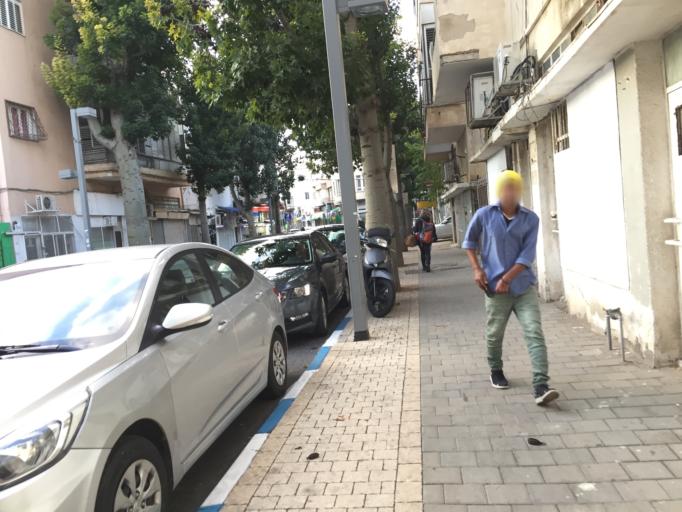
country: IL
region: Tel Aviv
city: Tel Aviv
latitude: 32.0584
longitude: 34.7742
